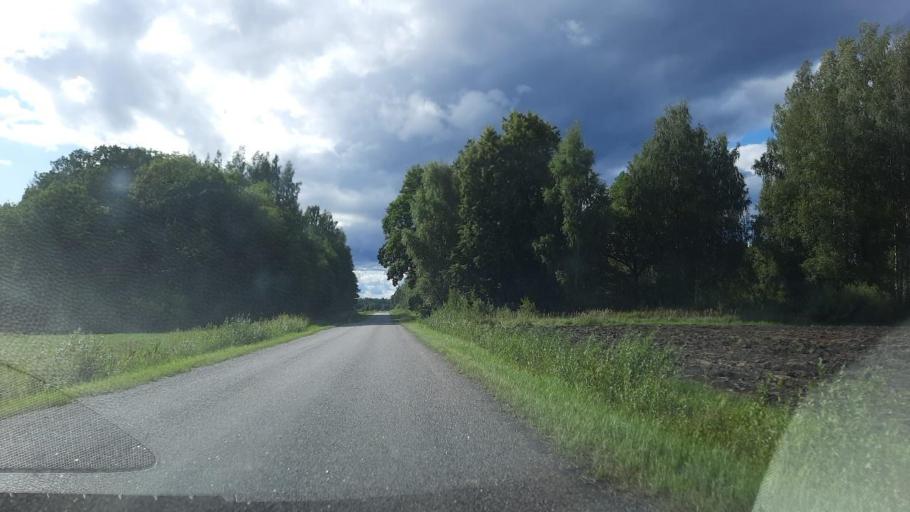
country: EE
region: Paernumaa
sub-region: Vaendra vald (alev)
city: Vandra
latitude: 58.4913
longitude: 24.9656
